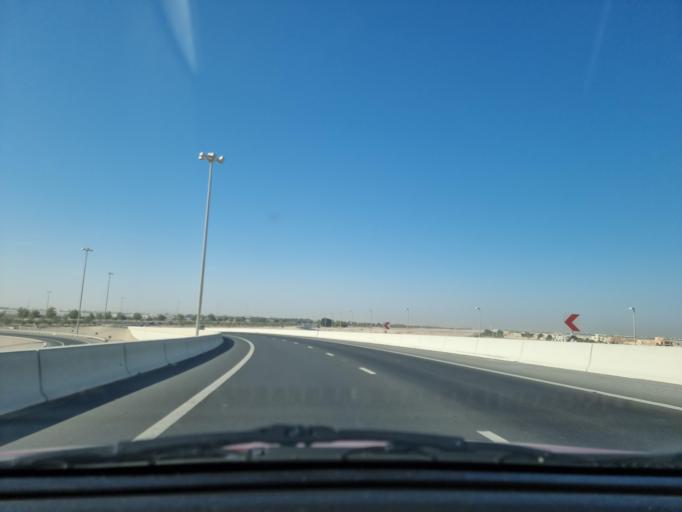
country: AE
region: Abu Dhabi
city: Abu Dhabi
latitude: 24.4172
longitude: 54.7130
